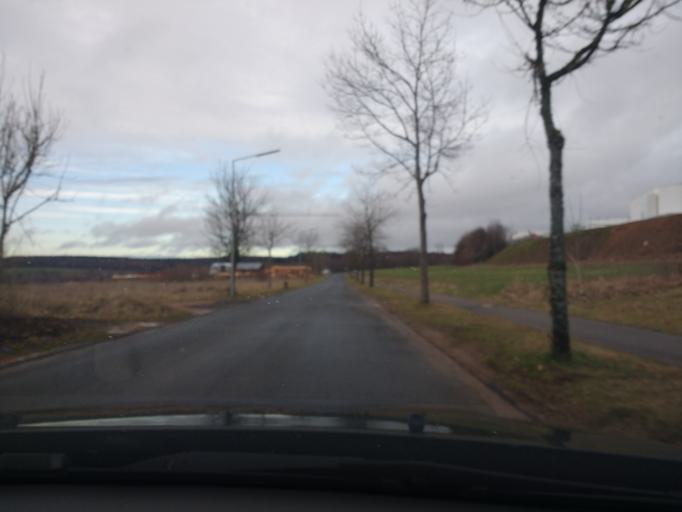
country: DE
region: Rheinland-Pfalz
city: Damflos
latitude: 49.6662
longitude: 6.9646
